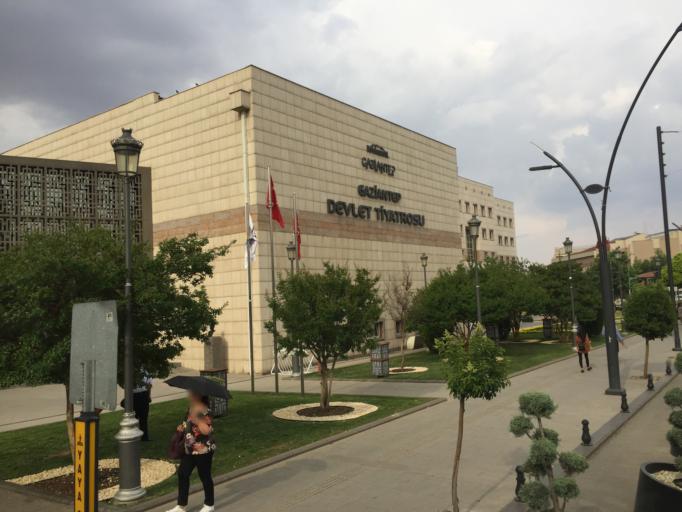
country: TR
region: Gaziantep
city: Gaziantep
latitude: 37.0658
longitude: 37.3726
